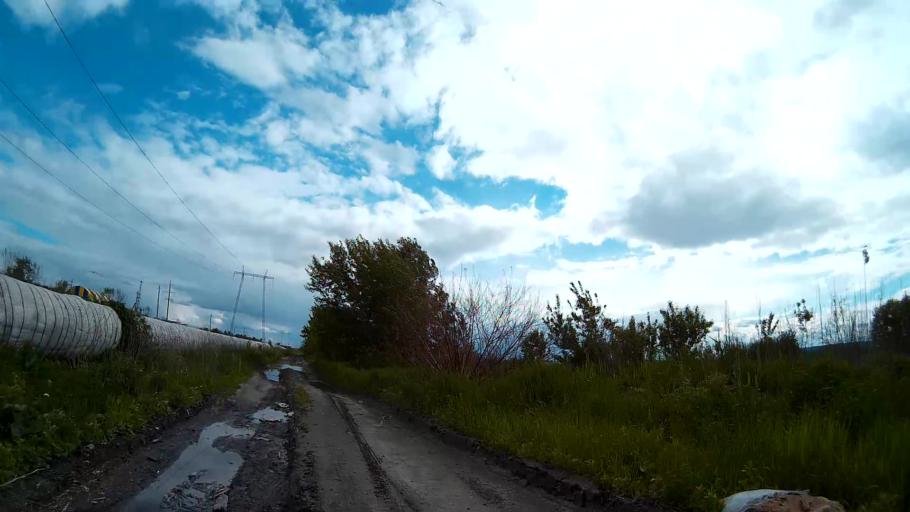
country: RU
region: Ulyanovsk
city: Novoul'yanovsk
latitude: 54.2363
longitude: 48.2954
